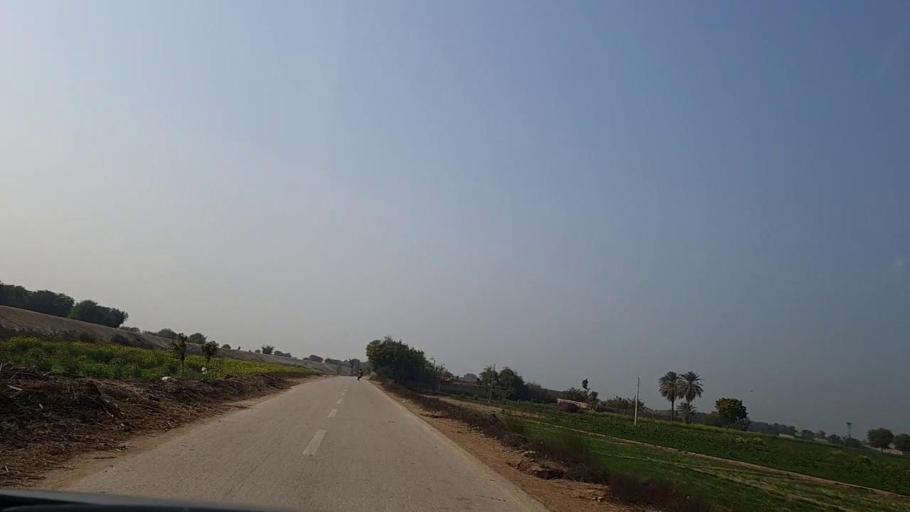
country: PK
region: Sindh
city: Sann
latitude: 26.1495
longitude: 68.1286
